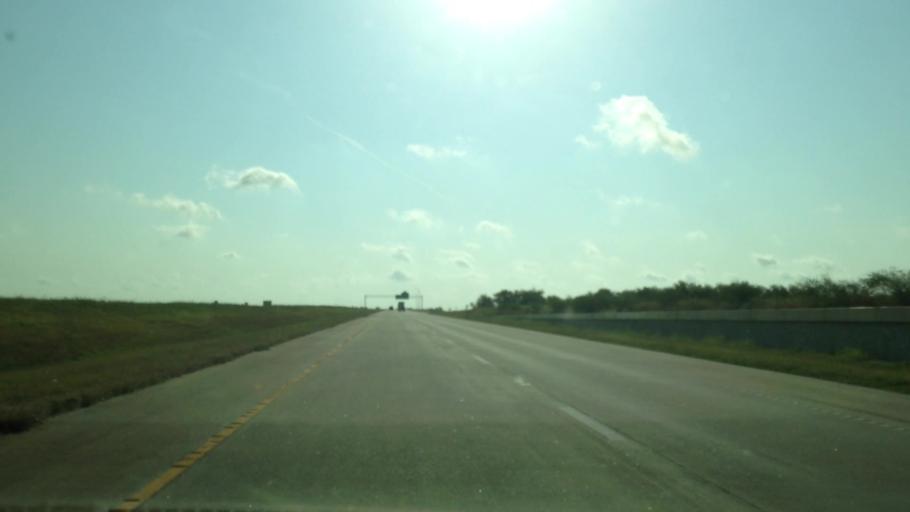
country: US
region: Texas
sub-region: Travis County
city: Onion Creek
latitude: 30.0813
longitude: -97.7186
